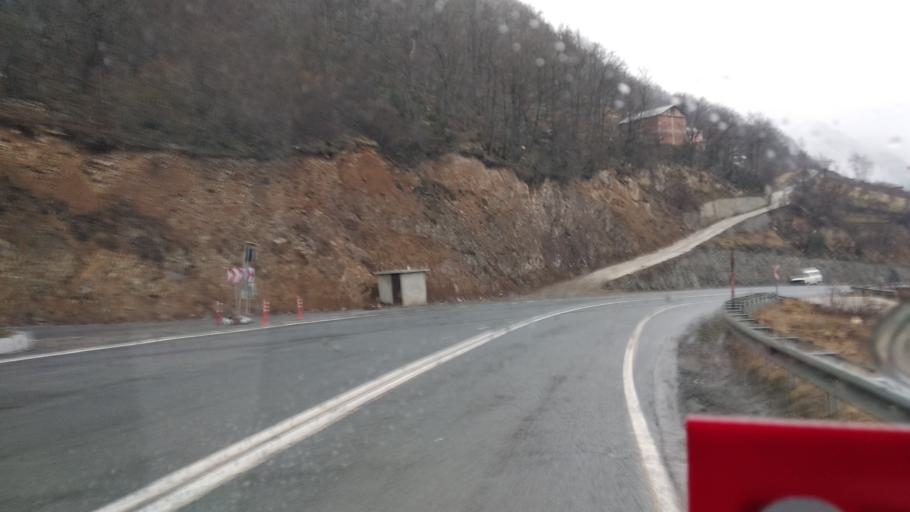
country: TR
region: Trabzon
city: Macka
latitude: 40.7173
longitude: 39.5146
